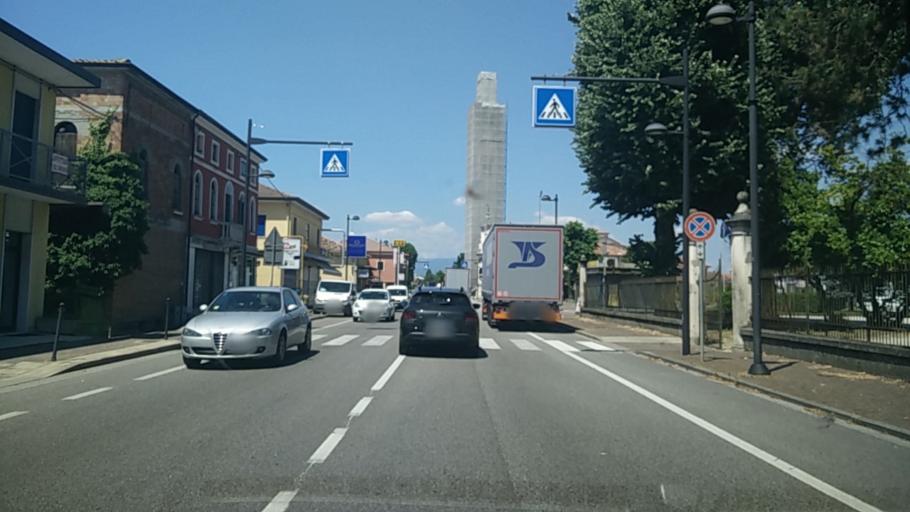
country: IT
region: Veneto
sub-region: Provincia di Padova
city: San Giorgio in Bosco
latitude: 45.5907
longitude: 11.8060
